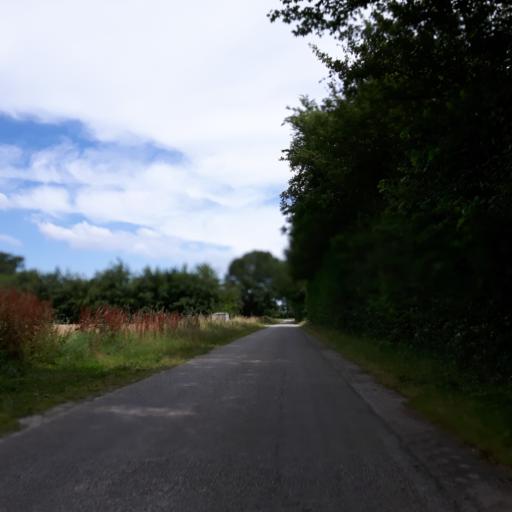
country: NL
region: Zeeland
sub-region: Schouwen-Duiveland
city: Bruinisse
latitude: 51.6418
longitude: 4.0543
